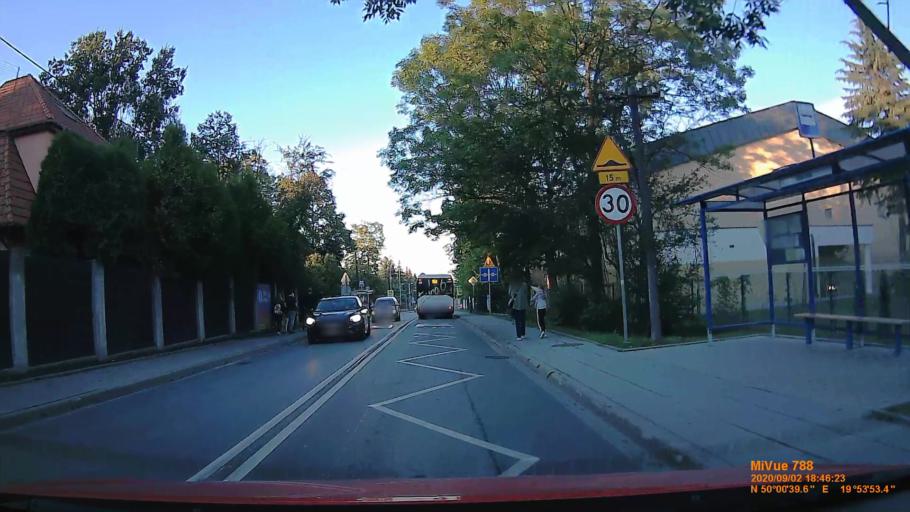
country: PL
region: Lesser Poland Voivodeship
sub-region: Krakow
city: Sidzina
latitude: 50.0112
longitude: 19.8984
